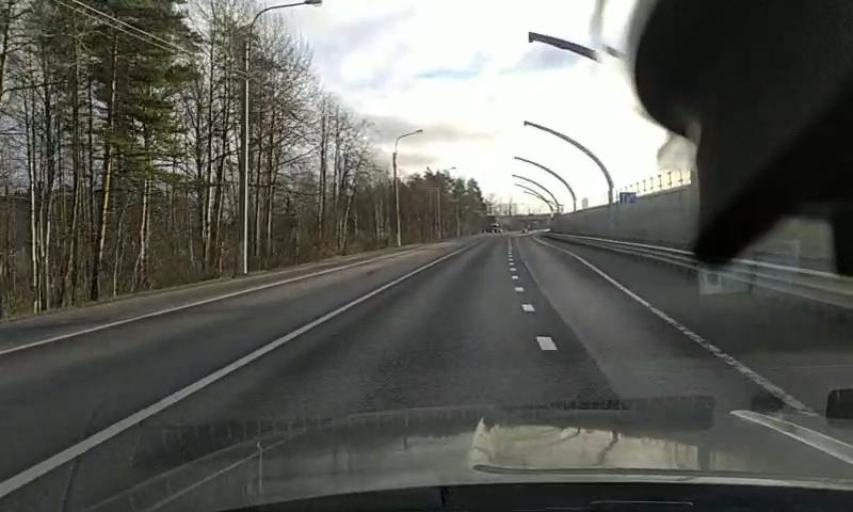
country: RU
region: St.-Petersburg
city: Solnechnoye
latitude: 60.1534
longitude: 29.9663
